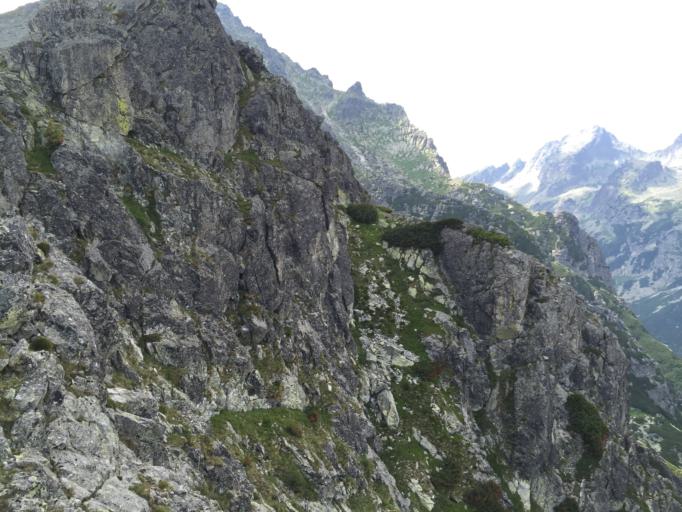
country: SK
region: Presovsky
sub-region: Okres Poprad
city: Vysoke Tatry
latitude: 49.1643
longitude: 20.2056
